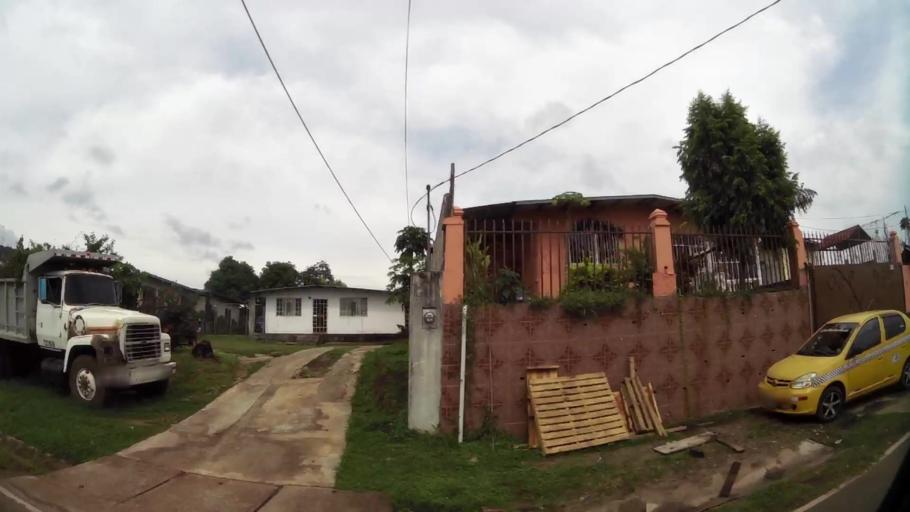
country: PA
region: Panama
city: Tocumen
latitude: 9.1120
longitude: -79.3790
